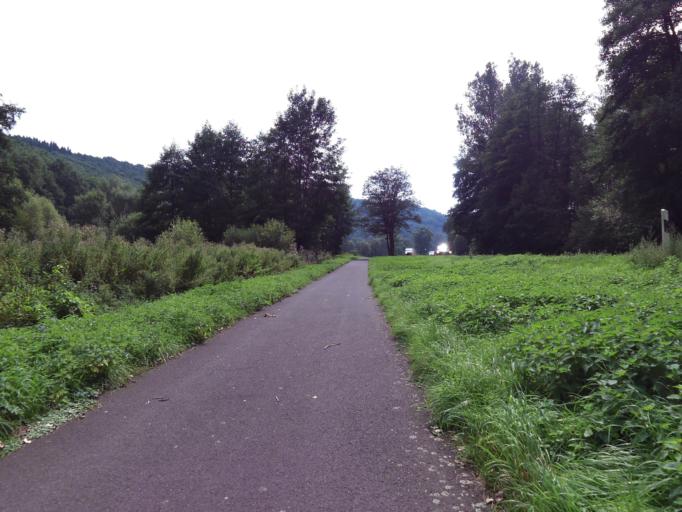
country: DE
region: Rheinland-Pfalz
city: Kalkofen
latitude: 49.7450
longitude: 7.8201
